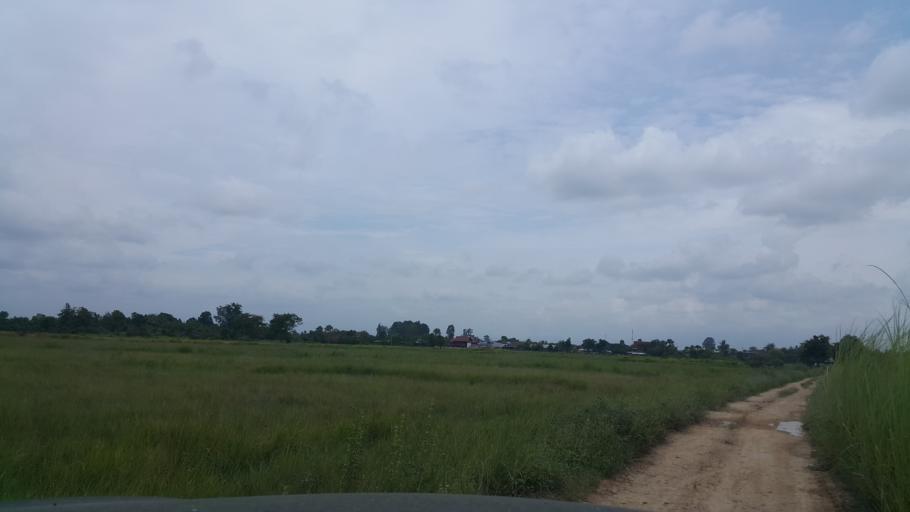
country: TH
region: Lamphun
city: Ban Thi
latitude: 18.6406
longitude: 99.1469
